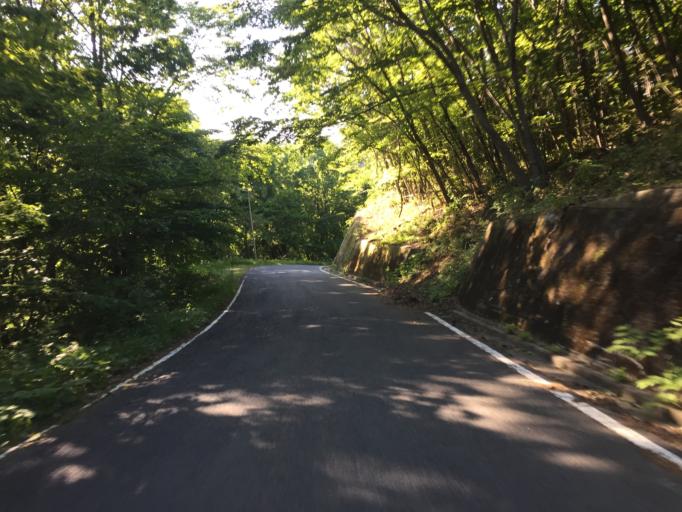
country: JP
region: Ibaraki
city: Kitaibaraki
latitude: 36.9125
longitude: 140.5801
